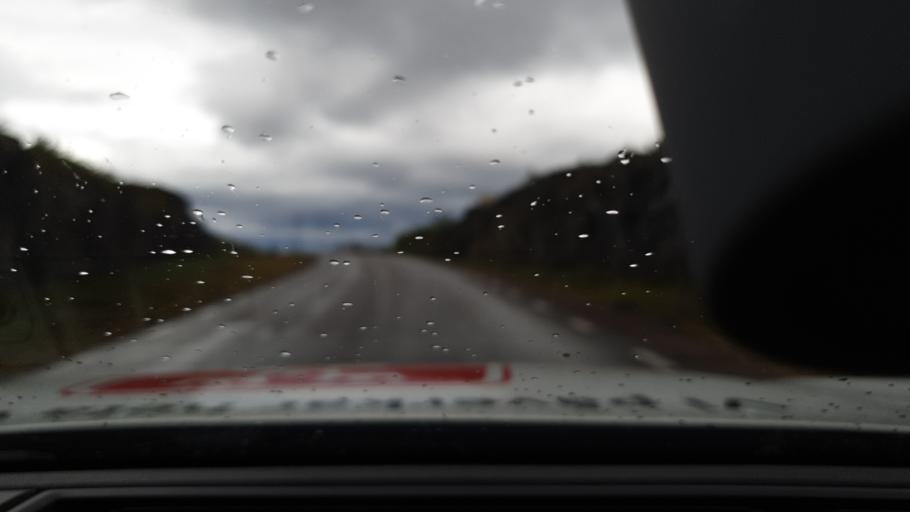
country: NO
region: Troms
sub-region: Bardu
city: Setermoen
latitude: 68.4273
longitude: 18.2797
